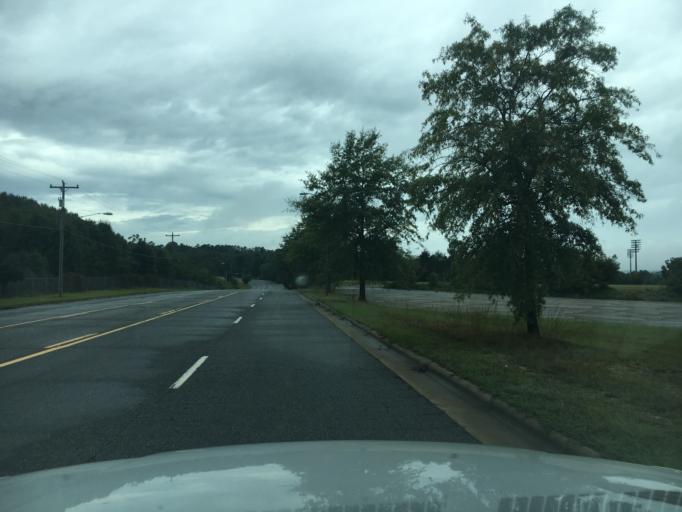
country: US
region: North Carolina
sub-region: Catawba County
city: Longview
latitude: 35.7471
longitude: -81.3756
